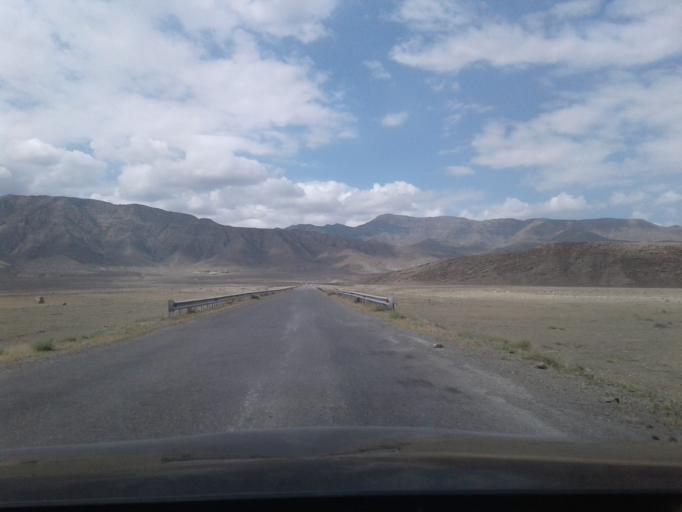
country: TM
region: Ahal
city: Baharly
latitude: 38.5109
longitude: 57.1304
